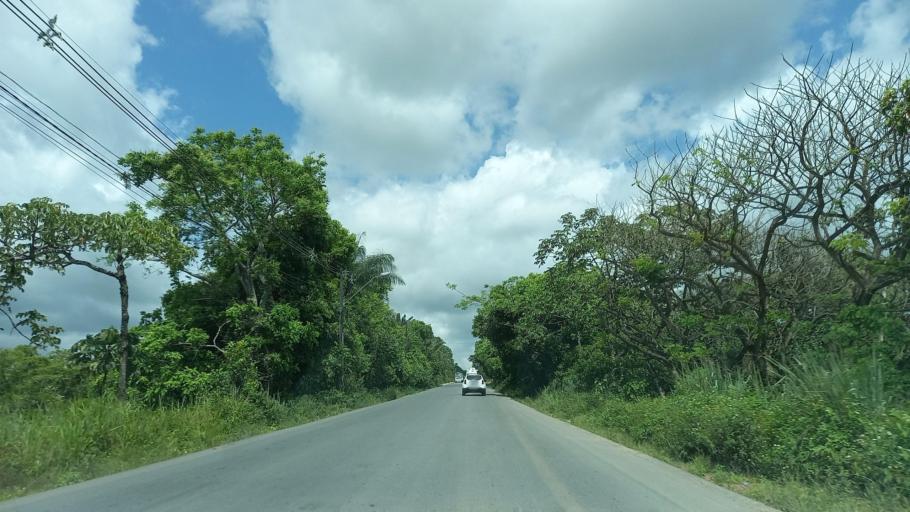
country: BR
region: Pernambuco
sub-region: Jaboatao Dos Guararapes
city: Jaboatao
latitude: -8.1602
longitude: -34.9934
